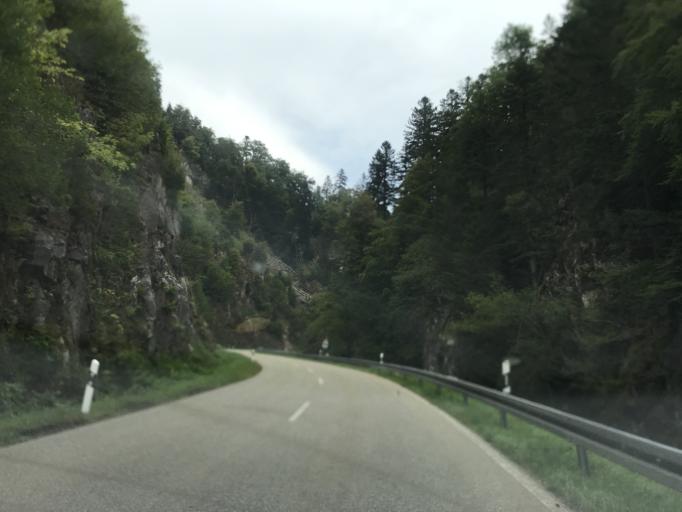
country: DE
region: Baden-Wuerttemberg
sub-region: Freiburg Region
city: Hasel
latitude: 47.6782
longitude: 7.9457
